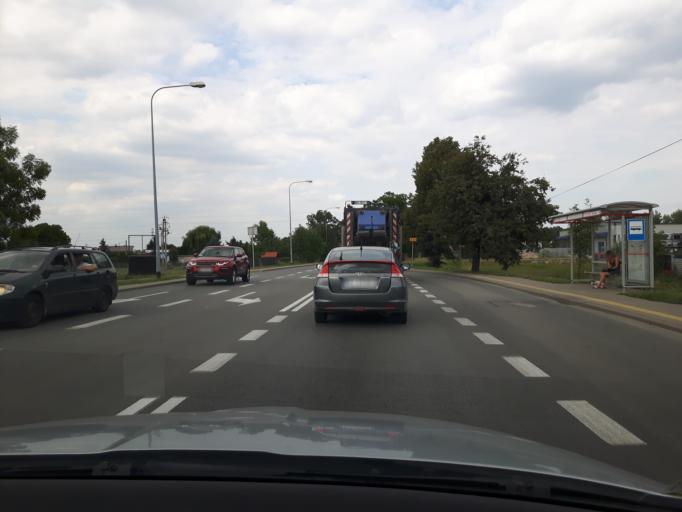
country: PL
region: Masovian Voivodeship
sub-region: Powiat legionowski
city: Stanislawow Pierwszy
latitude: 52.3560
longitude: 21.0286
